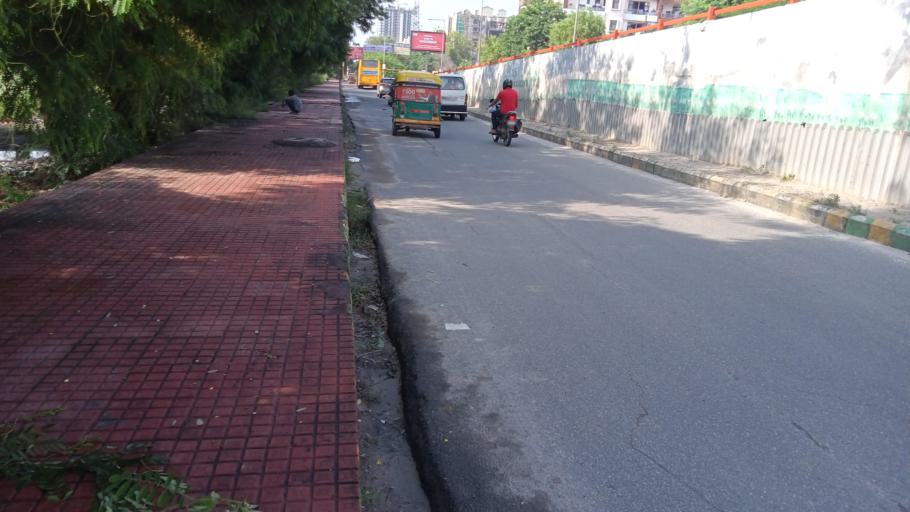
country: IN
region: Uttar Pradesh
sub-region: Ghaziabad
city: Ghaziabad
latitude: 28.6604
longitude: 77.3745
